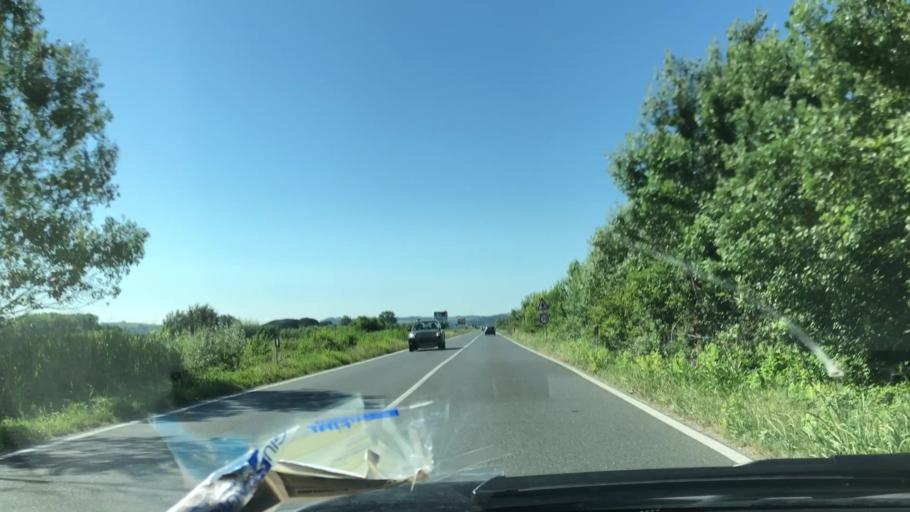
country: IT
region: Tuscany
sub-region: Province of Pisa
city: Forcoli
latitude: 43.5968
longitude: 10.6972
